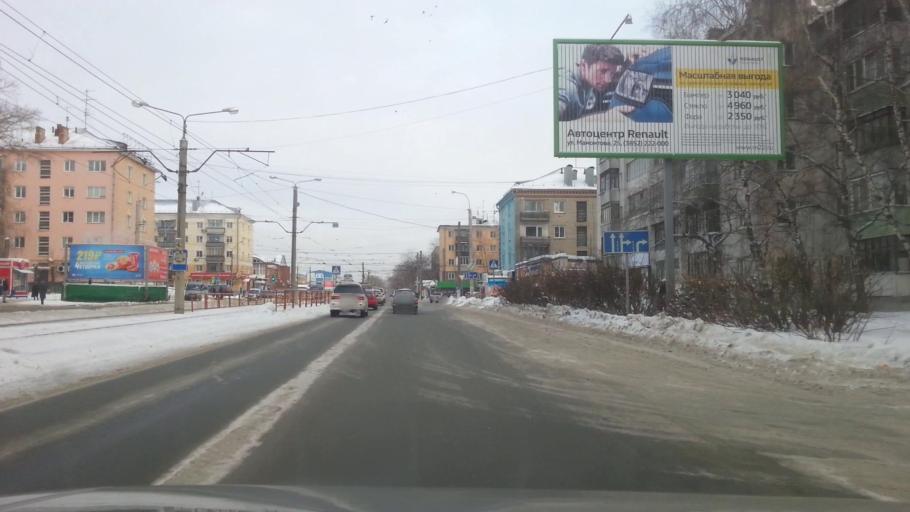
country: RU
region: Altai Krai
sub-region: Gorod Barnaulskiy
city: Barnaul
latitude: 53.3725
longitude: 83.7480
